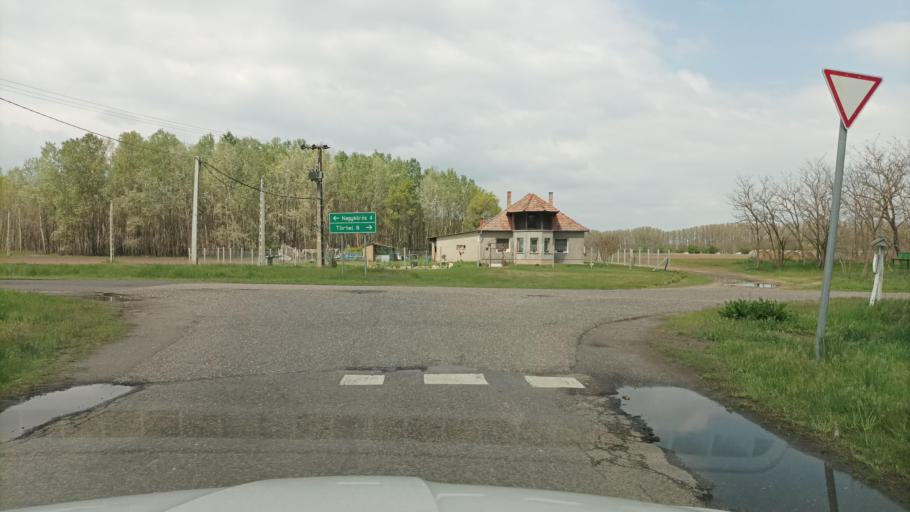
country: HU
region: Pest
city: Nagykoros
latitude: 47.0550
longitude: 19.8506
